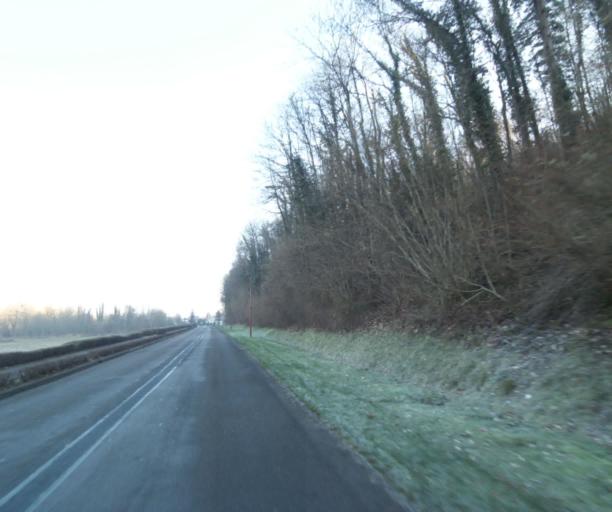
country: FR
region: Champagne-Ardenne
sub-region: Departement de la Haute-Marne
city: Bienville
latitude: 48.5473
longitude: 5.0753
